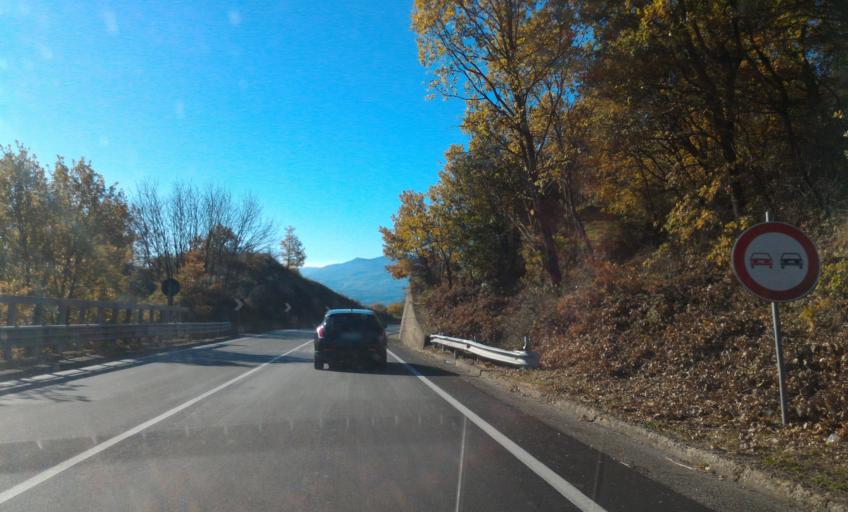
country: IT
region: Calabria
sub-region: Provincia di Cosenza
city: Rovito
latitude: 39.3060
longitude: 16.3235
